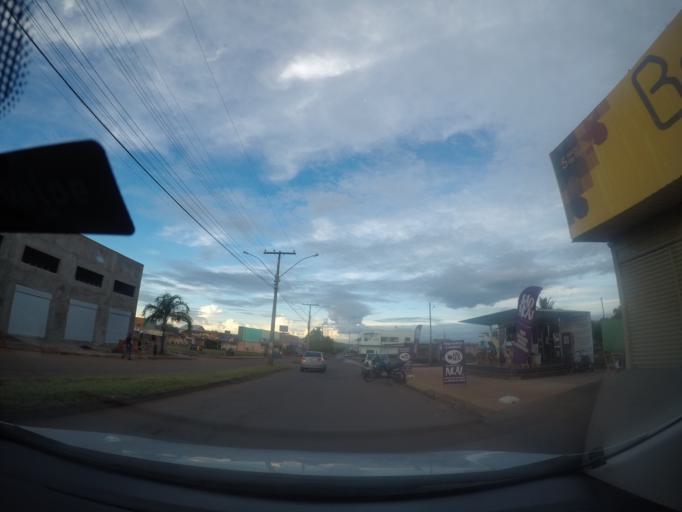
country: BR
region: Goias
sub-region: Goianira
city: Goianira
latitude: -16.5770
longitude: -49.3871
